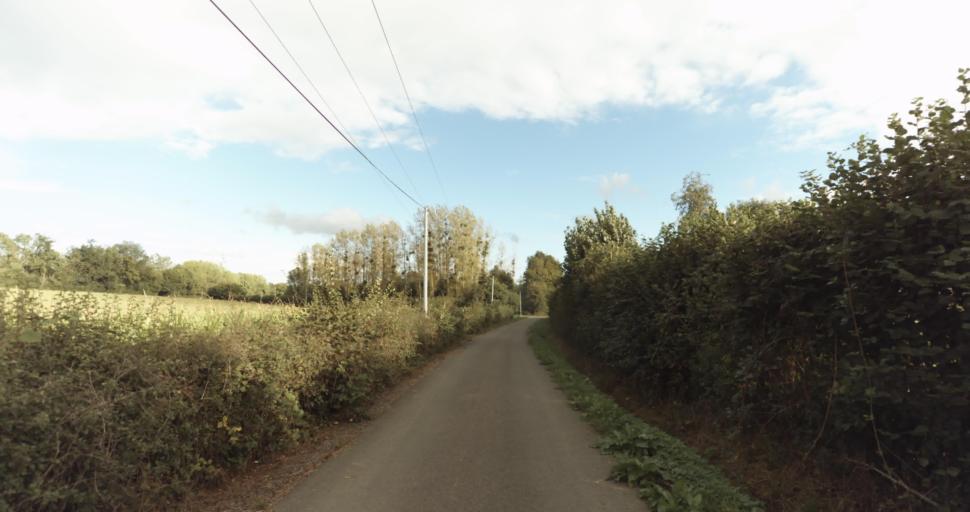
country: FR
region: Lower Normandy
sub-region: Departement de l'Orne
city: Sainte-Gauburge-Sainte-Colombe
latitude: 48.7221
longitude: 0.4216
